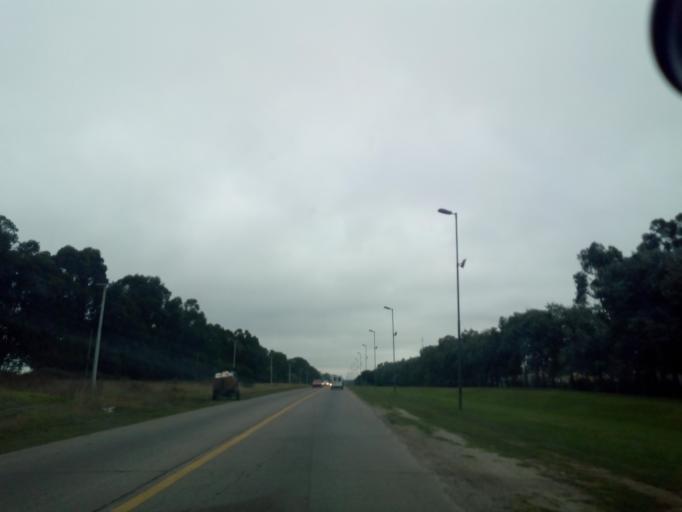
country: AR
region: Buenos Aires
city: Mar del Plata
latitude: -38.0732
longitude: -57.5765
